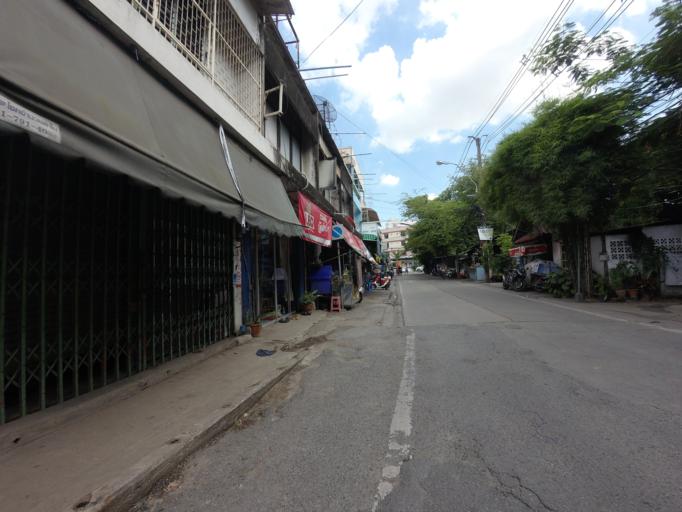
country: TH
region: Bangkok
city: Lak Si
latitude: 13.8581
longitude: 100.5853
